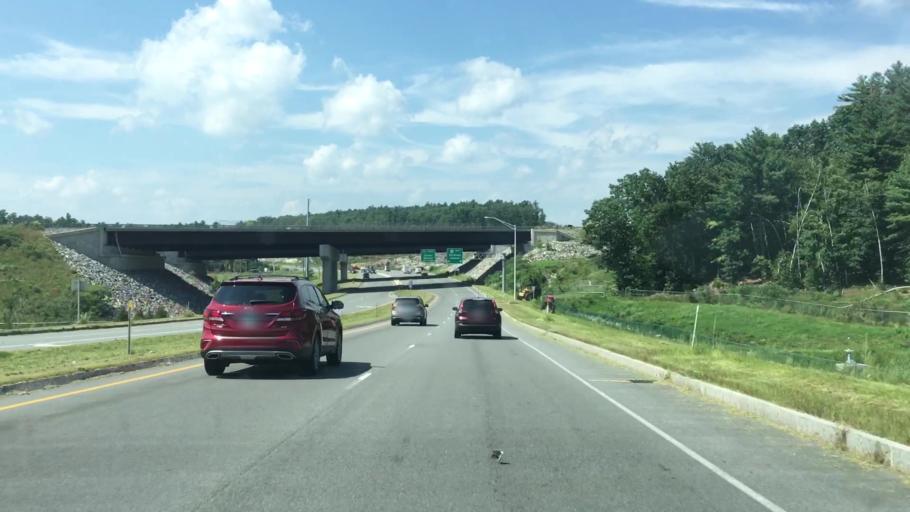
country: US
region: New Hampshire
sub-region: Rockingham County
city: Windham
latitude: 42.8085
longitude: -71.2693
